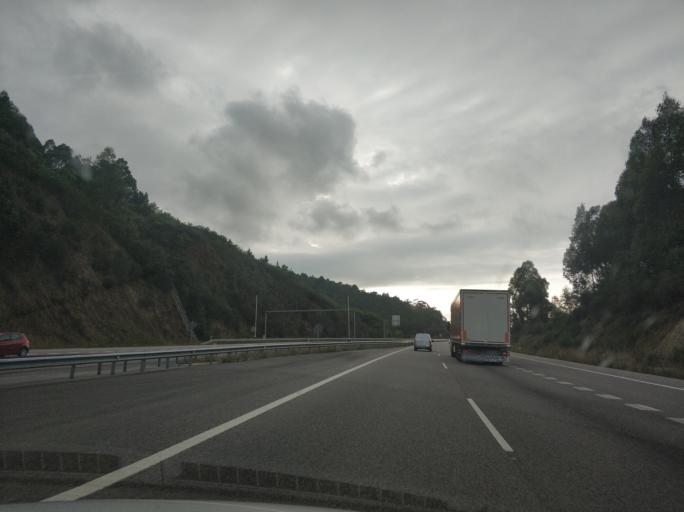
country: ES
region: Asturias
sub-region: Province of Asturias
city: Muros de Nalon
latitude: 43.5401
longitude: -6.1256
